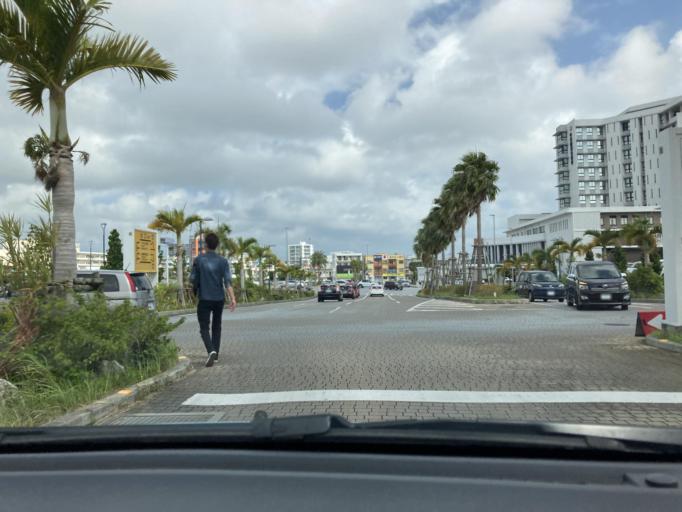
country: JP
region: Okinawa
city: Okinawa
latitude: 26.3153
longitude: 127.7964
